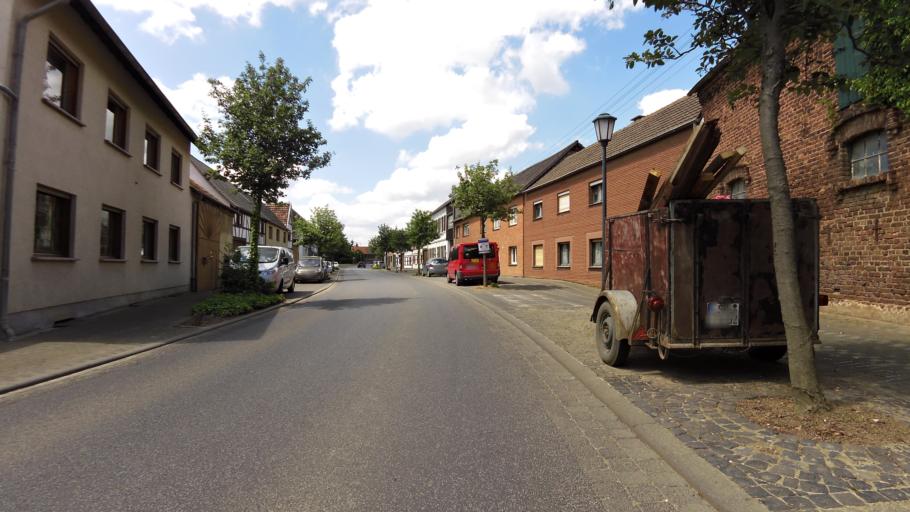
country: DE
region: North Rhine-Westphalia
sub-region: Regierungsbezirk Koln
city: Rheinbach
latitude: 50.6414
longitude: 6.9659
